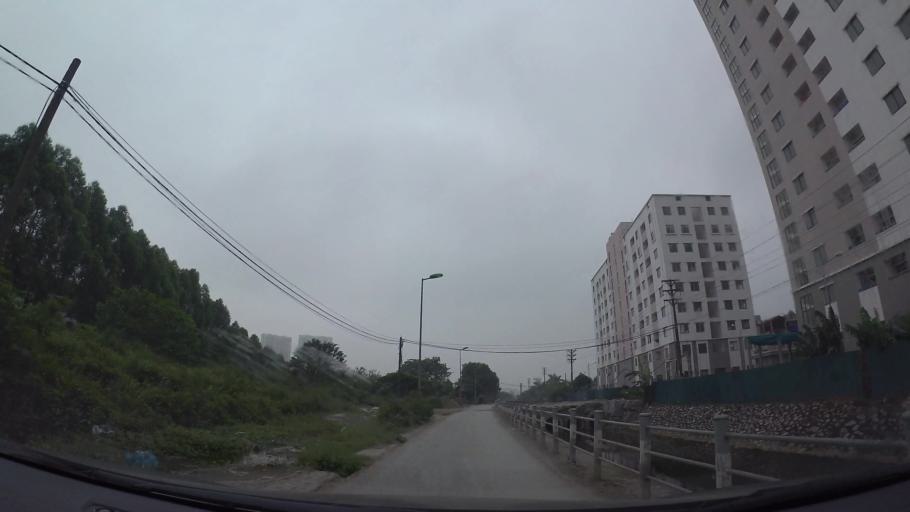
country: VN
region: Ha Noi
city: Van Dien
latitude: 20.9767
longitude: 105.8782
